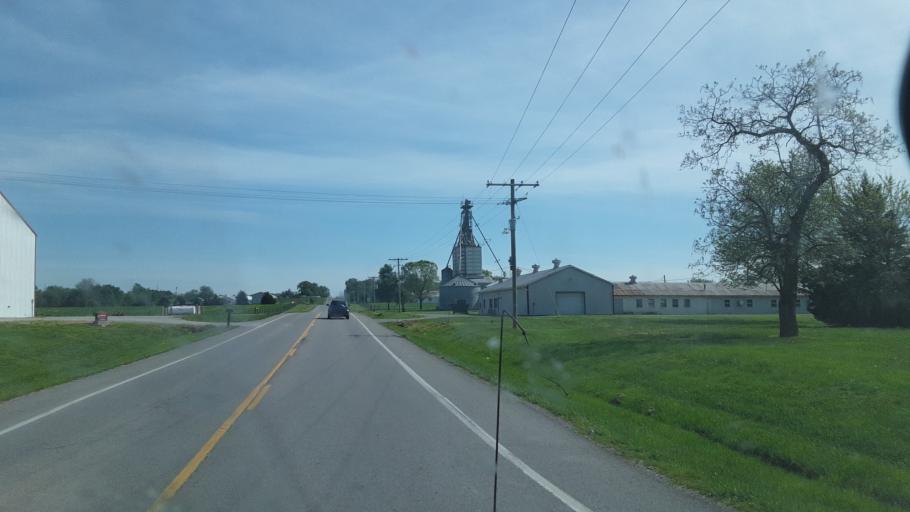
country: US
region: Illinois
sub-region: Jackson County
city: Carbondale
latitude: 37.7010
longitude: -89.2471
